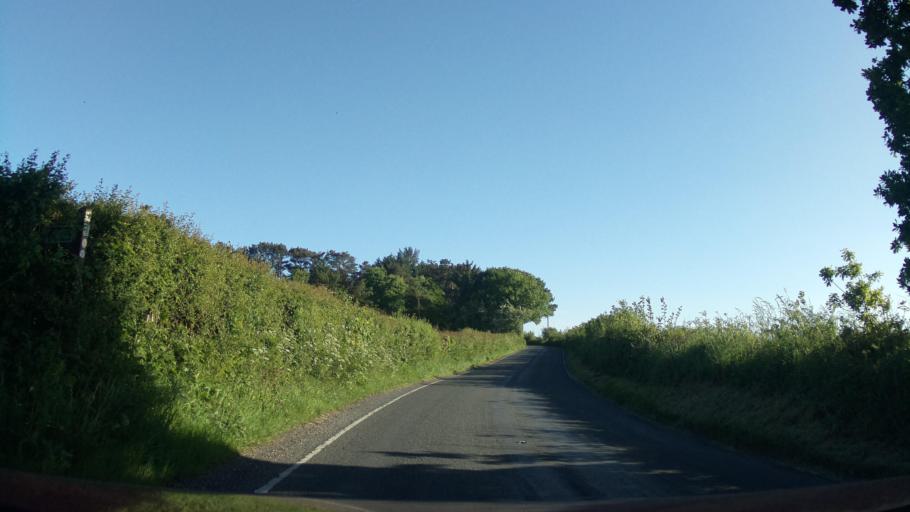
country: GB
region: England
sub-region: Devon
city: Axminster
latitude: 50.7402
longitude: -2.9873
